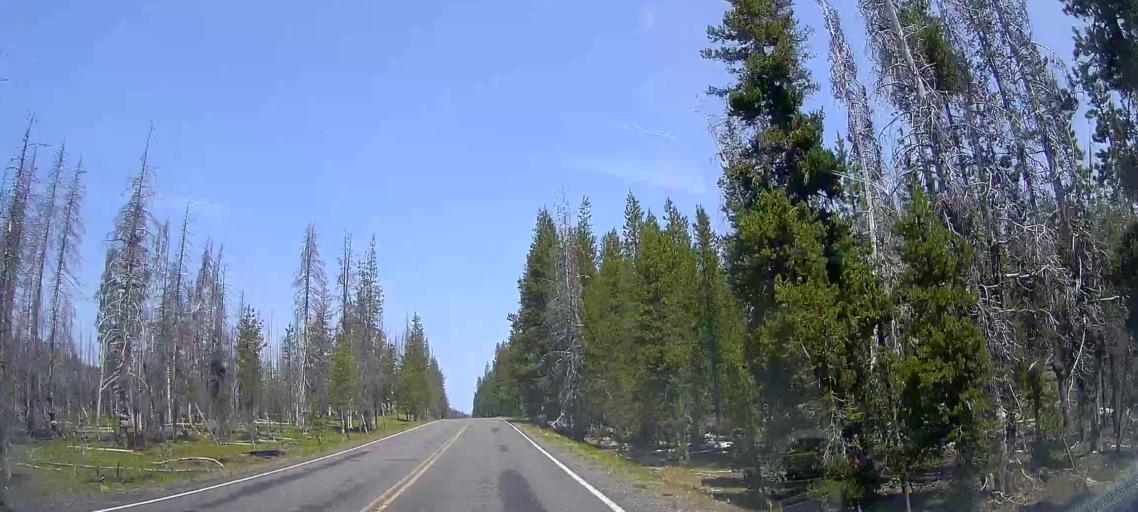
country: US
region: Oregon
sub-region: Lane County
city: Oakridge
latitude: 43.0484
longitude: -122.1201
